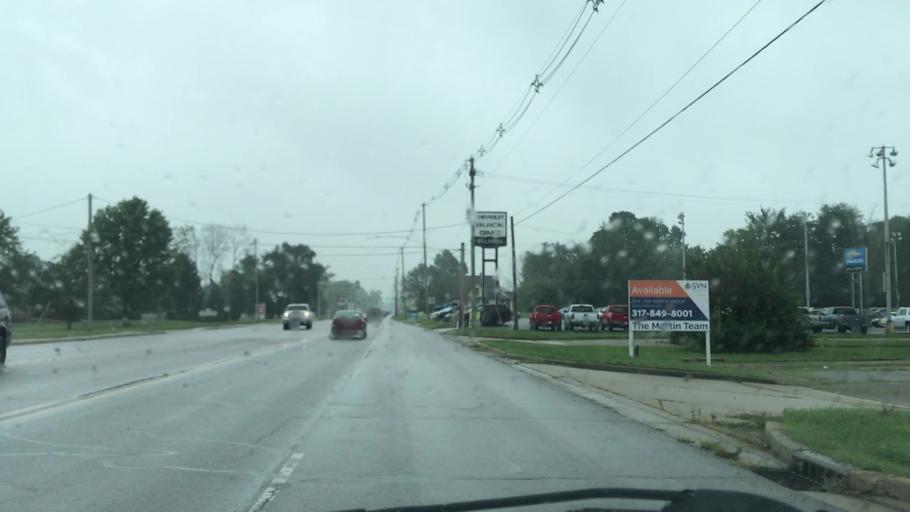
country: US
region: Indiana
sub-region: Boone County
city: Lebanon
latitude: 40.0646
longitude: -86.4725
